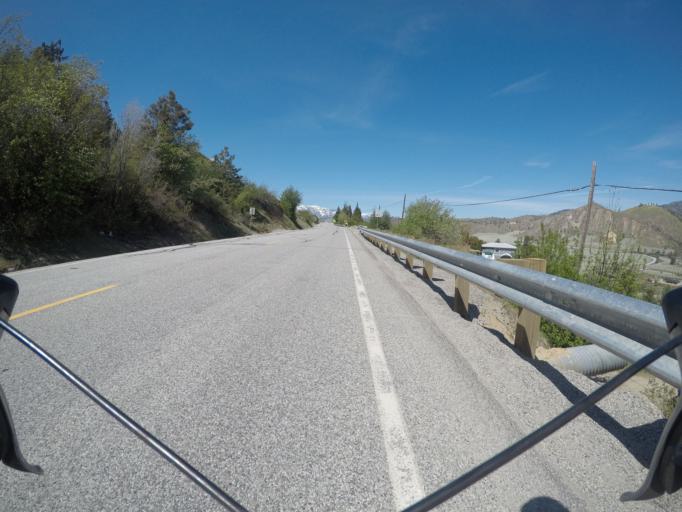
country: US
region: Washington
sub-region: Chelan County
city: Cashmere
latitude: 47.5289
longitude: -120.5116
